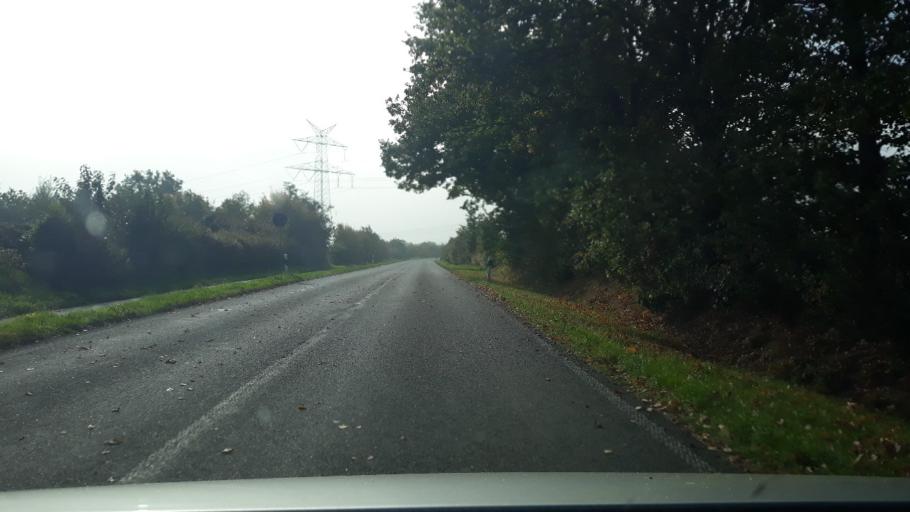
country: DE
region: Schleswig-Holstein
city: Gross Rheide
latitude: 54.4397
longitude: 9.4278
